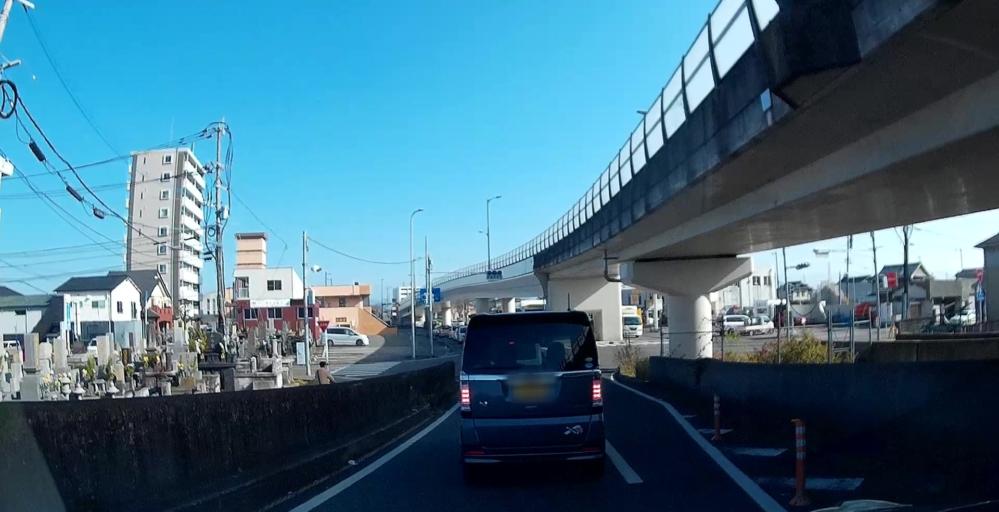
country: JP
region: Kumamoto
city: Kumamoto
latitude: 32.7714
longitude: 130.6928
